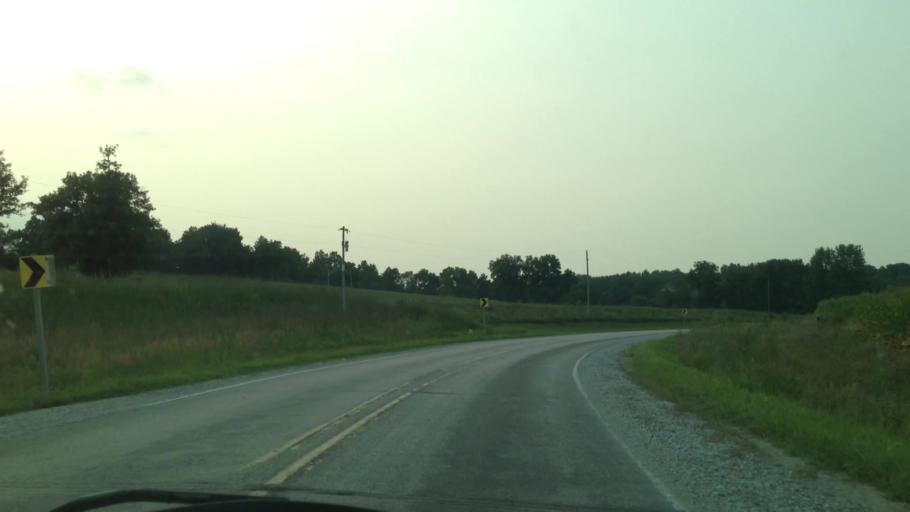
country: US
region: Iowa
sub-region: Iowa County
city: Marengo
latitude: 41.8290
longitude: -92.0820
